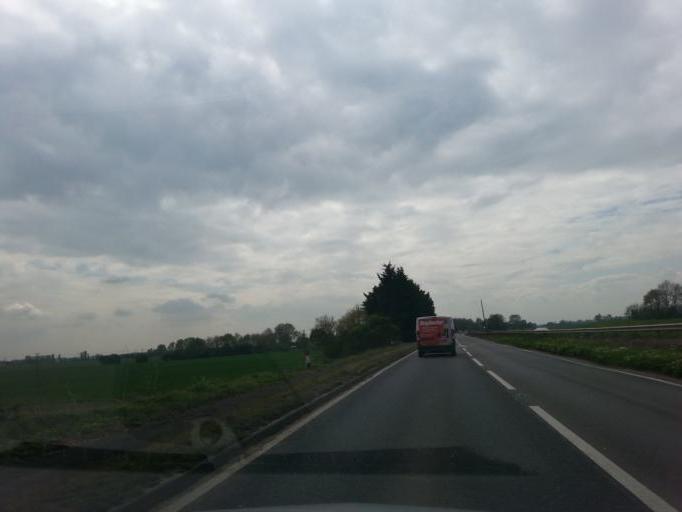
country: GB
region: England
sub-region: Cambridgeshire
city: Wisbech
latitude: 52.6394
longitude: 0.1266
